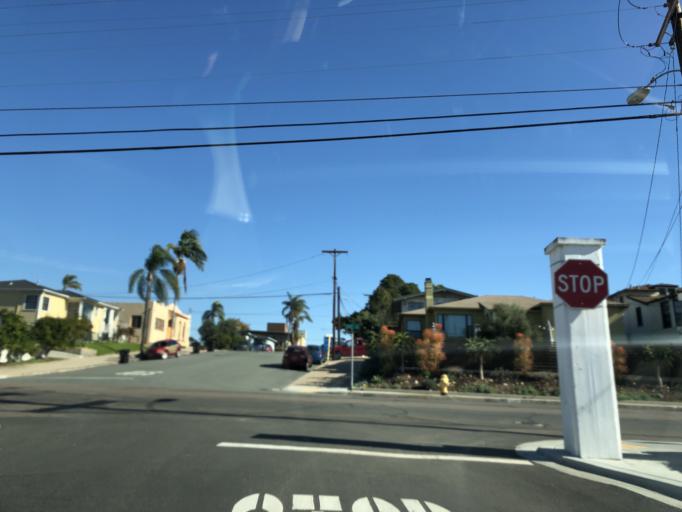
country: US
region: California
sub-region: San Diego County
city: San Diego
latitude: 32.7285
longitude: -117.1323
